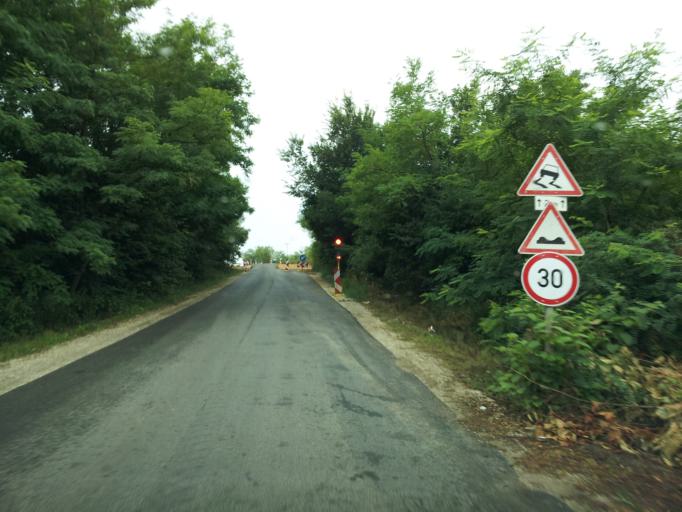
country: HU
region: Vas
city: Kormend
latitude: 46.9637
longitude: 16.6283
